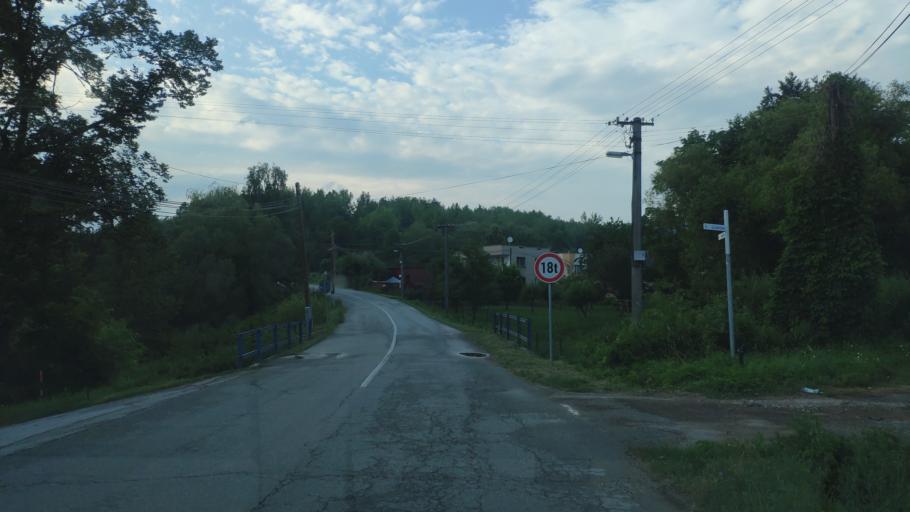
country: SK
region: Kosicky
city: Moldava nad Bodvou
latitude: 48.6877
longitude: 20.9751
